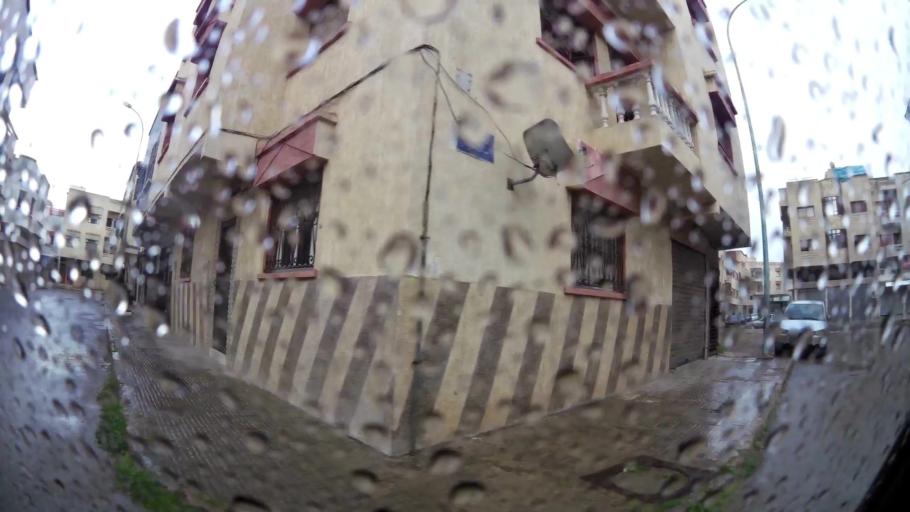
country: MA
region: Doukkala-Abda
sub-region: El-Jadida
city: El Jadida
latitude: 33.2460
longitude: -8.5249
